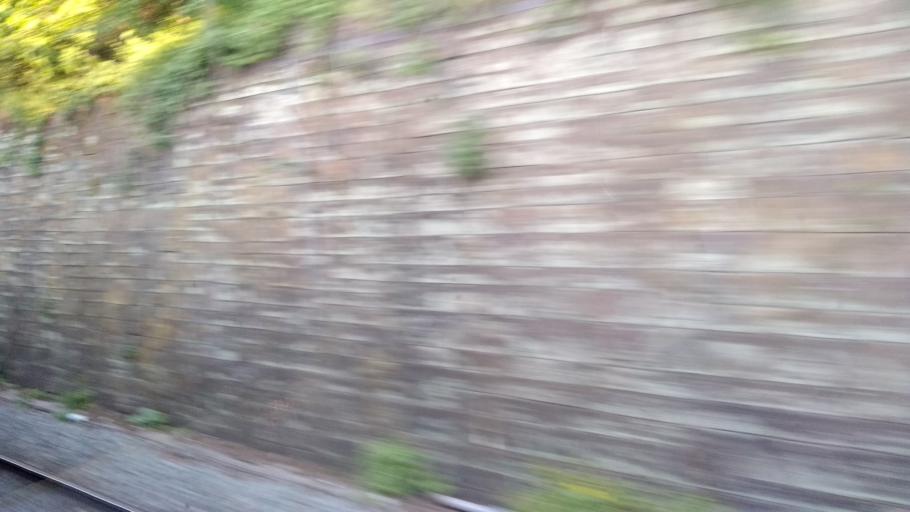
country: GB
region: England
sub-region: Bristol
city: Bristol
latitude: 51.4550
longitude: -2.5664
